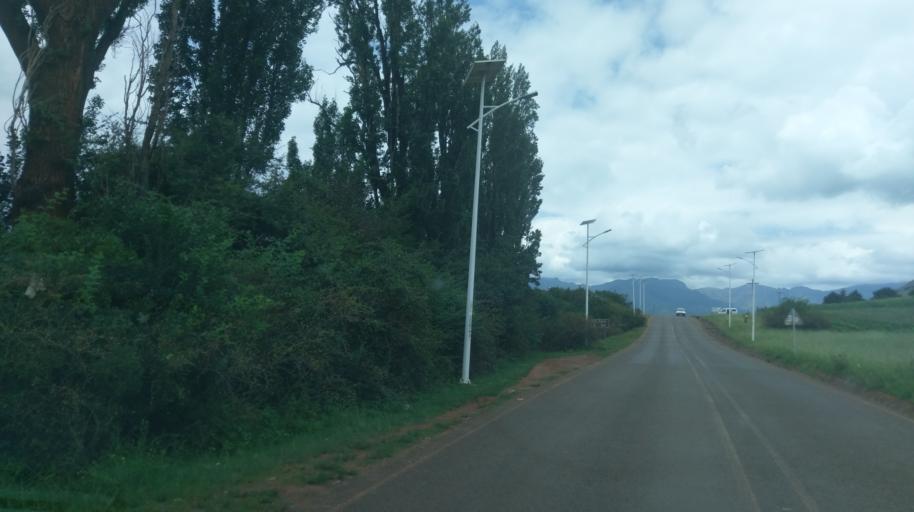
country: LS
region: Leribe
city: Leribe
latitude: -29.0111
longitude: 28.2160
